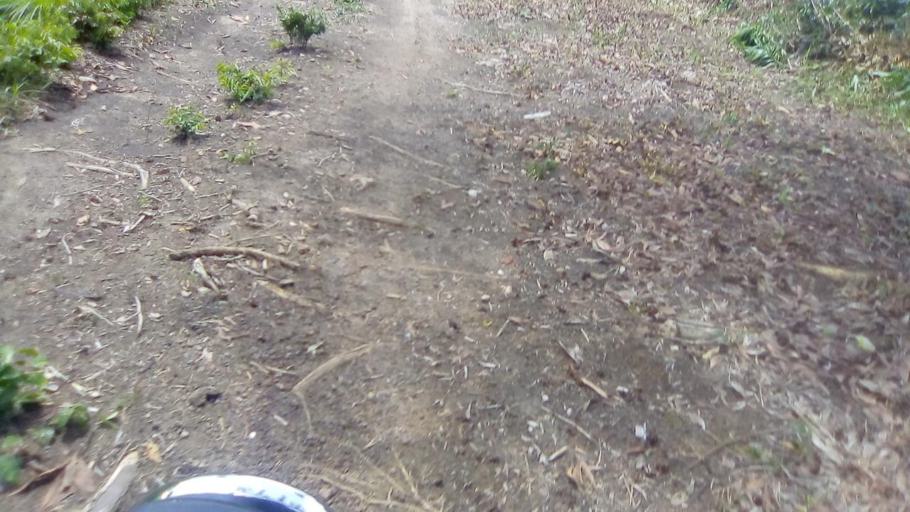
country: SL
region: Southern Province
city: Bo
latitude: 7.9297
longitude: -11.7449
